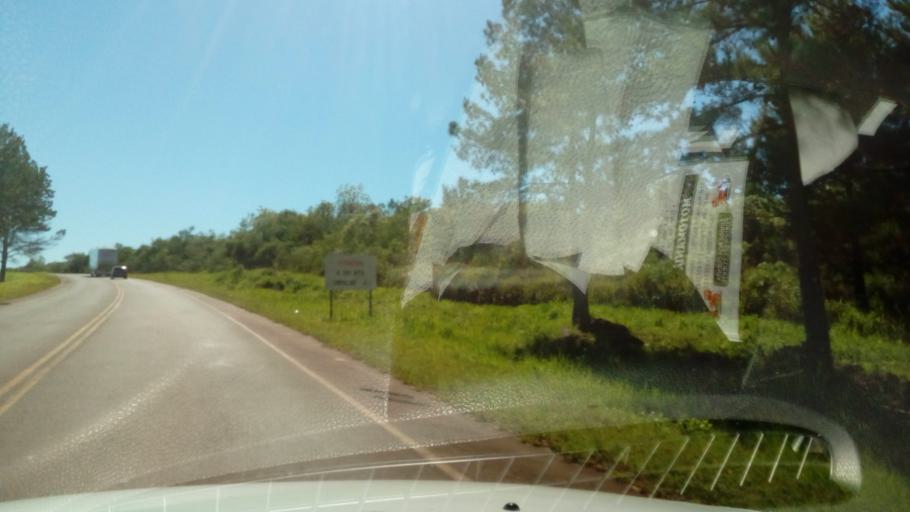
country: AR
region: Misiones
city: Santa Ana
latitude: -27.4175
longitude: -55.5314
